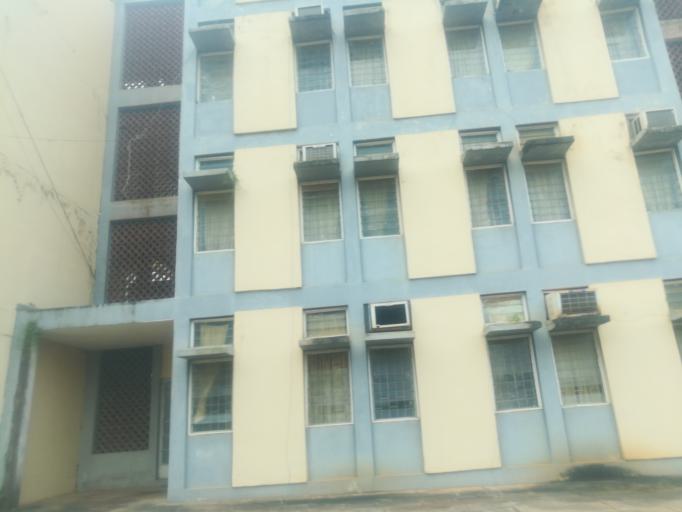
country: NG
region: Oyo
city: Ibadan
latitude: 7.4110
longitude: 3.9045
